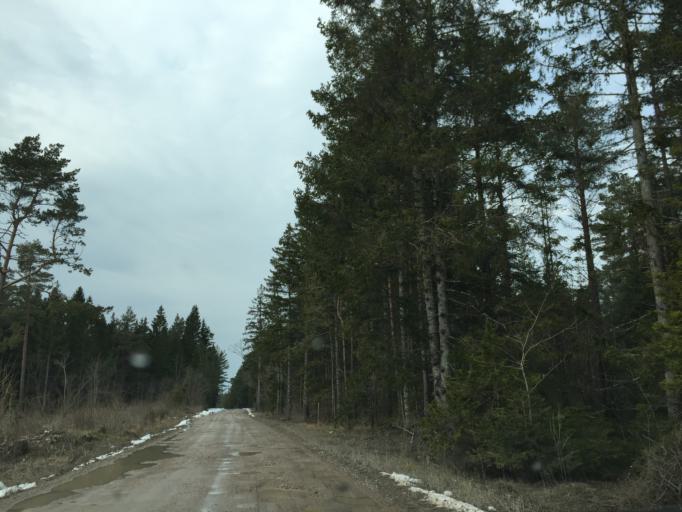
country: EE
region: Saare
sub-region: Kuressaare linn
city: Kuressaare
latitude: 58.4263
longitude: 22.1496
